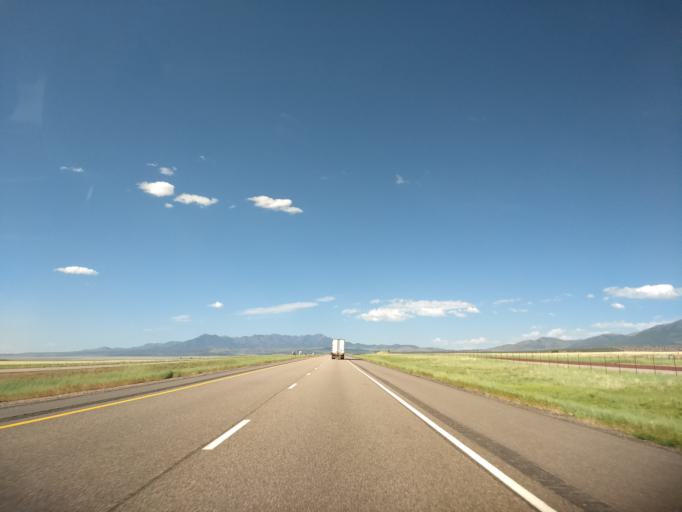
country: US
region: Utah
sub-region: Millard County
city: Fillmore
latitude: 39.0387
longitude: -112.2956
